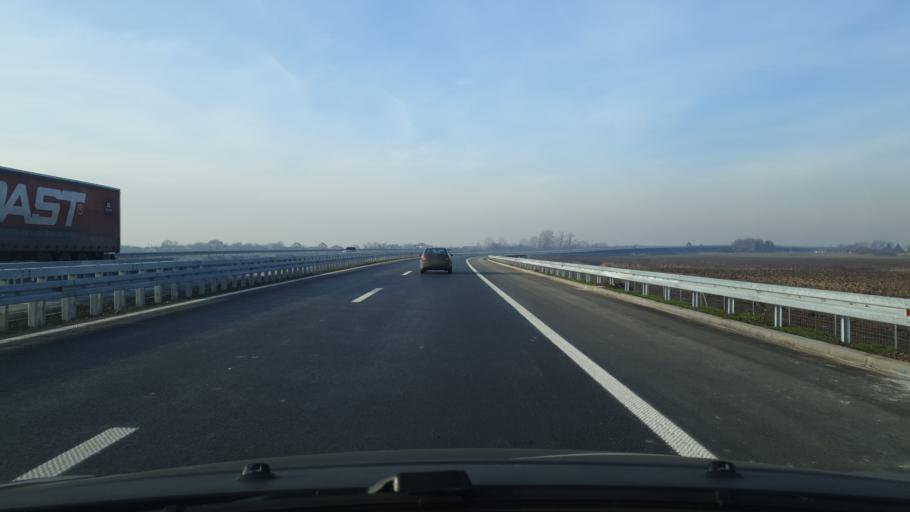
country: RS
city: Boljevci
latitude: 44.7261
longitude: 20.2524
